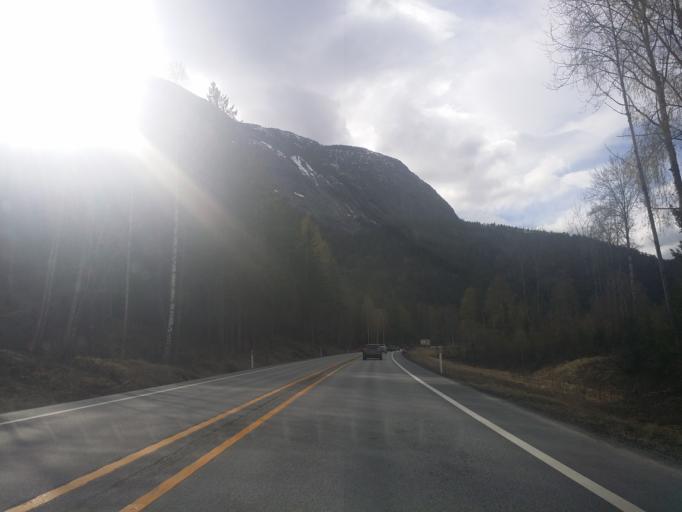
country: NO
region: Buskerud
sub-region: Fla
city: Fla
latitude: 60.4441
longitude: 9.2899
